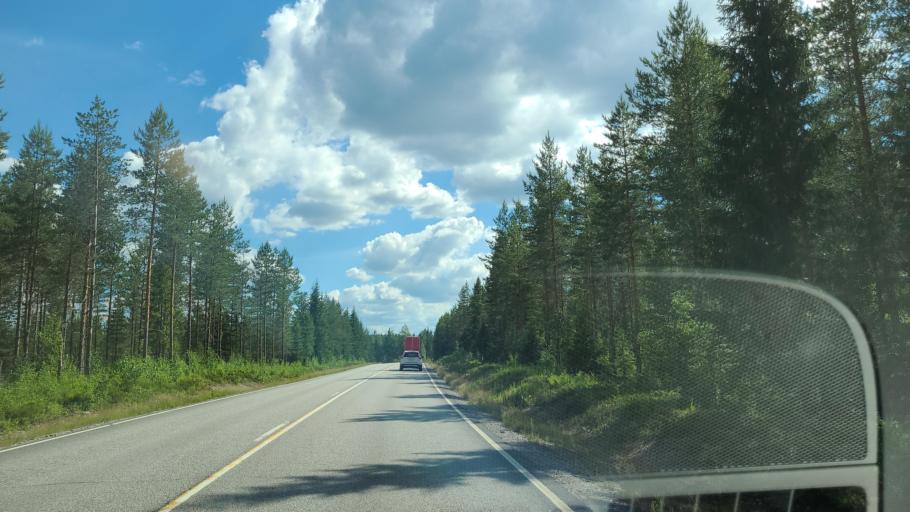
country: FI
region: Central Finland
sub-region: Keuruu
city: Multia
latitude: 62.4690
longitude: 24.7069
